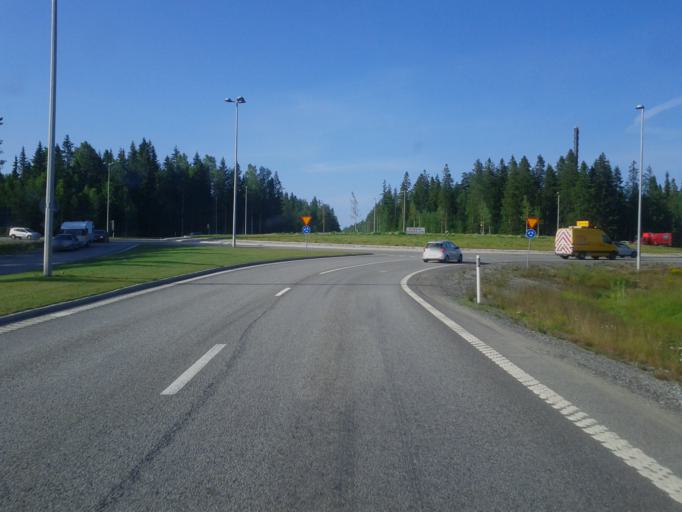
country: SE
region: Vaesterbotten
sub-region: Umea Kommun
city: Ersmark
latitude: 63.8466
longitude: 20.3415
